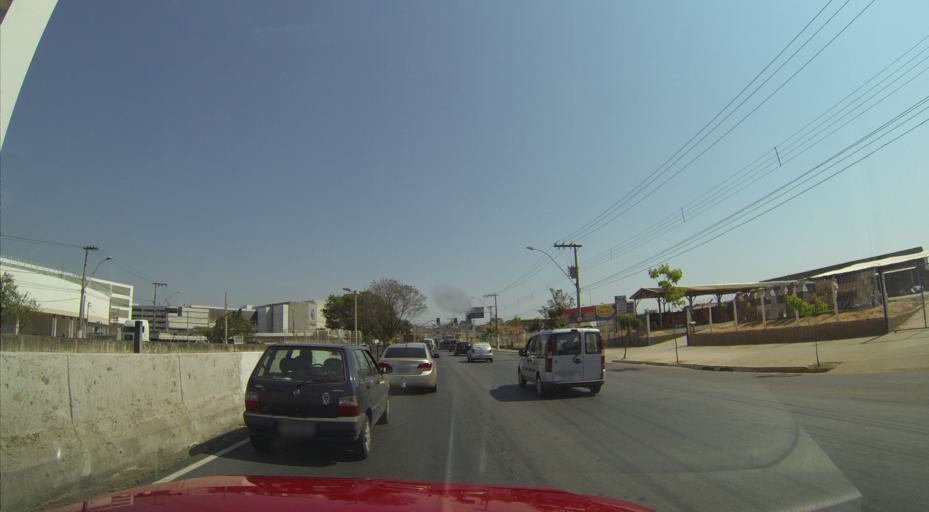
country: BR
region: Minas Gerais
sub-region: Belo Horizonte
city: Belo Horizonte
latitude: -19.8232
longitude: -43.9447
